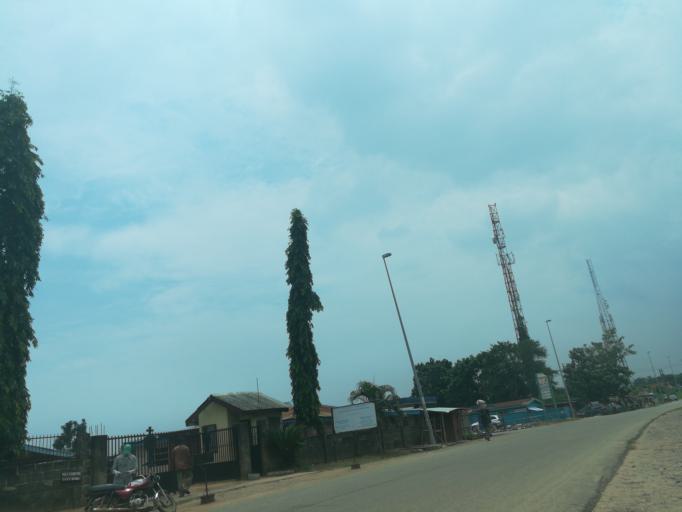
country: NG
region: Lagos
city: Ikorodu
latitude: 6.5633
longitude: 3.6037
